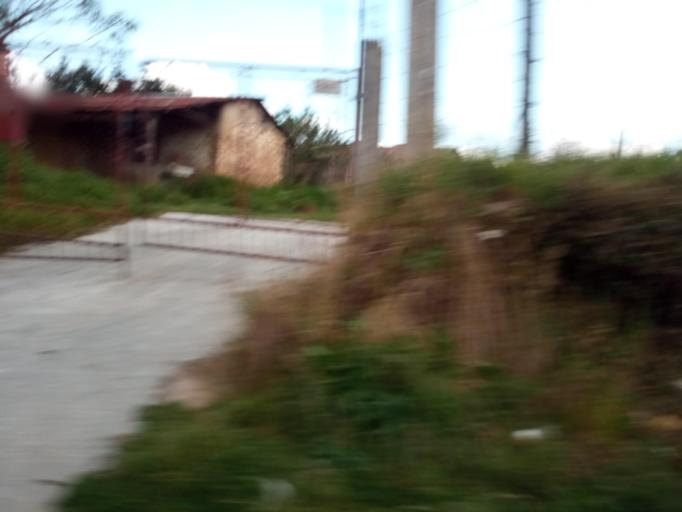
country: GT
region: Quetzaltenango
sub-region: Municipio de La Esperanza
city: La Esperanza
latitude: 14.8554
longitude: -91.5499
